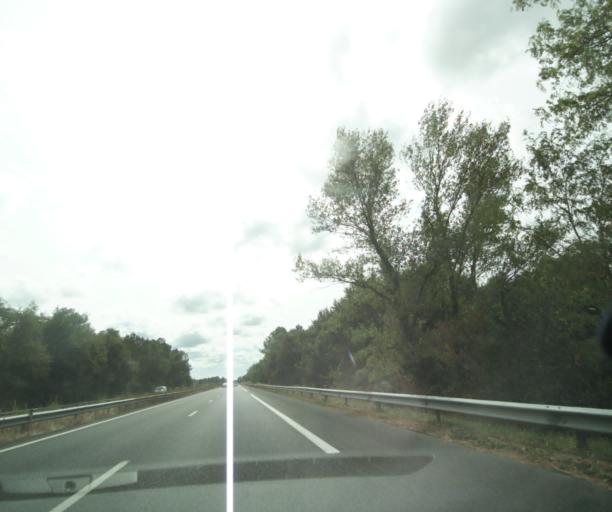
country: FR
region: Aquitaine
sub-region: Departement de la Gironde
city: Marcillac
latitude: 45.2483
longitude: -0.5381
